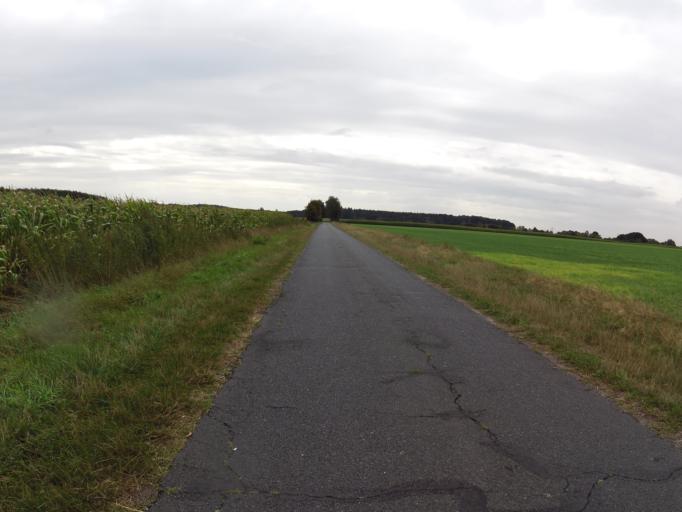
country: DE
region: Lower Saxony
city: Scheessel
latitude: 53.1924
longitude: 9.4687
